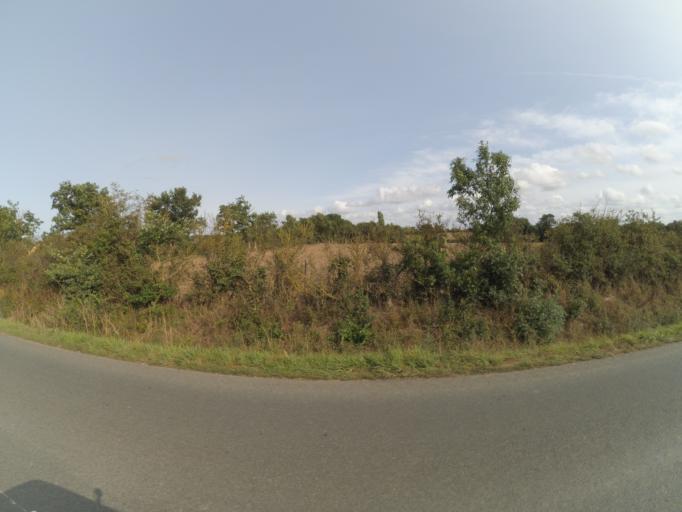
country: FR
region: Pays de la Loire
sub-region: Departement de la Vendee
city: La Guyonniere
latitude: 46.9717
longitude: -1.2451
